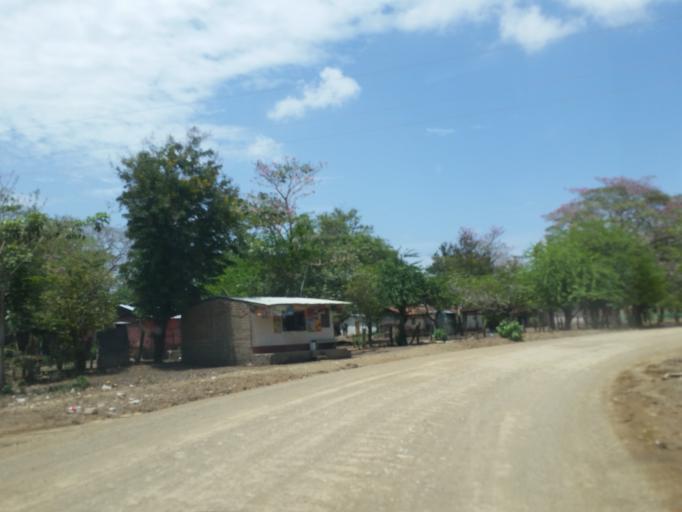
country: NI
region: Rivas
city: Tola
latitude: 11.4538
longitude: -86.0678
